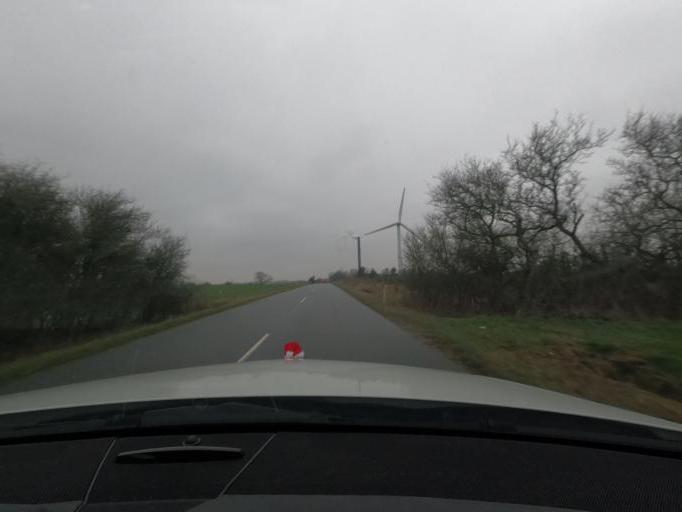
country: DK
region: South Denmark
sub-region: Haderslev Kommune
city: Haderslev
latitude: 55.1972
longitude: 9.4628
